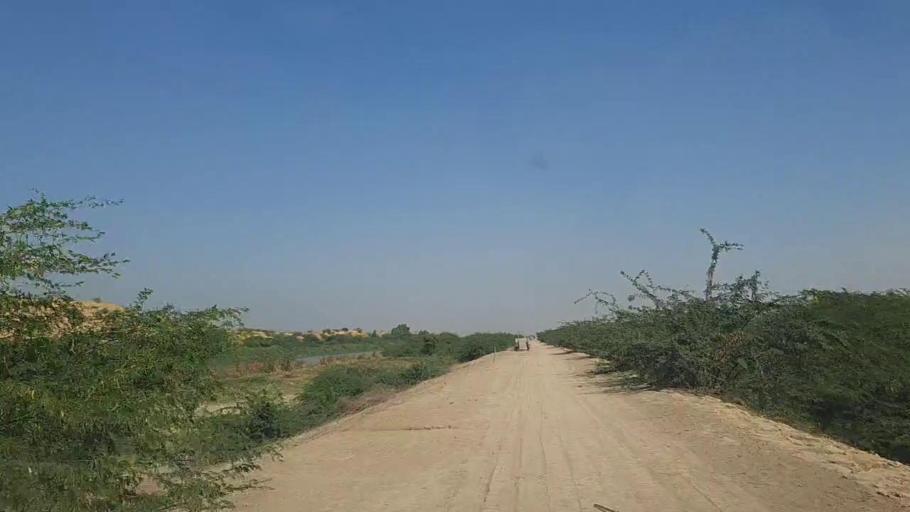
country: PK
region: Sindh
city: Daro Mehar
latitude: 24.8705
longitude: 68.0472
